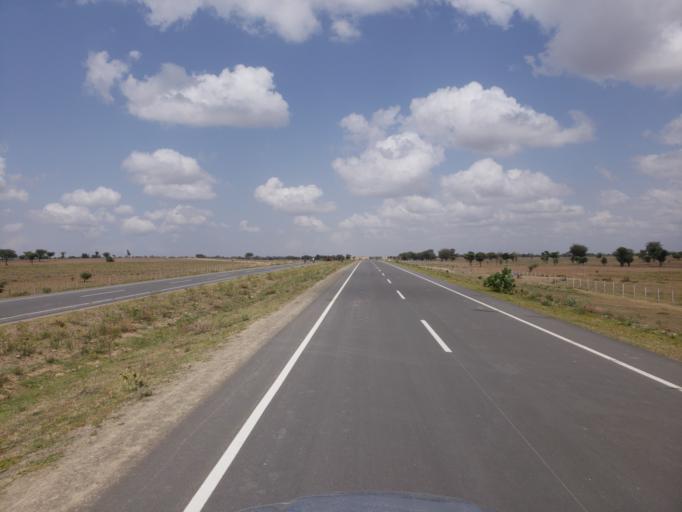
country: ET
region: Oromiya
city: Mojo
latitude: 8.3213
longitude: 38.9550
